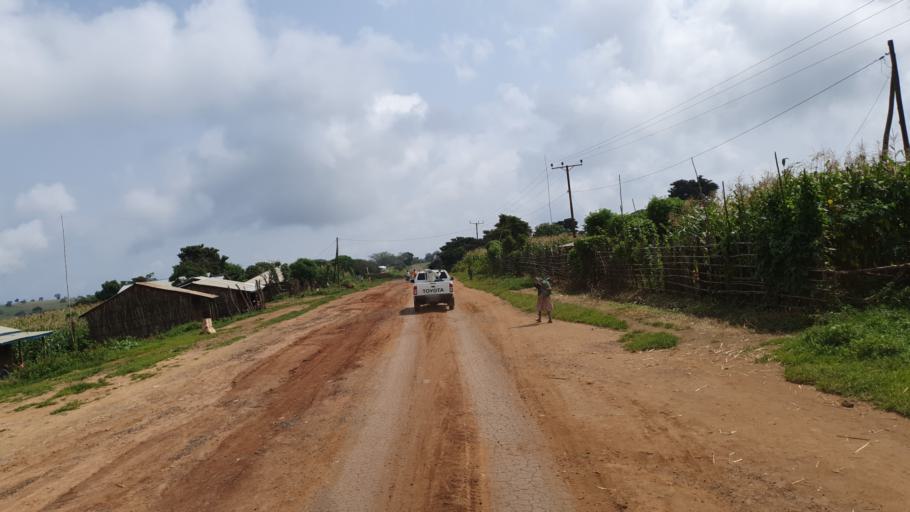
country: ET
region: Amhara
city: Bure
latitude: 10.1885
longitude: 36.9632
